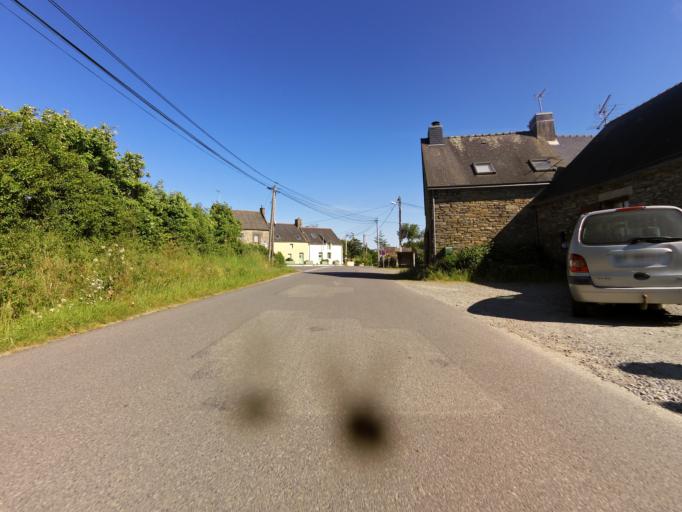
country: FR
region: Brittany
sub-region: Departement du Morbihan
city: Penestin
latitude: 47.4701
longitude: -2.4571
